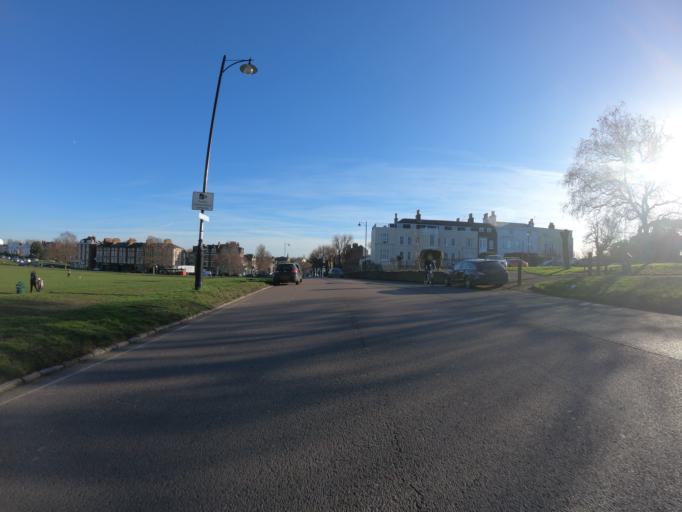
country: GB
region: England
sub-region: Greater London
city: Blackheath
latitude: 51.4677
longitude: 0.0054
